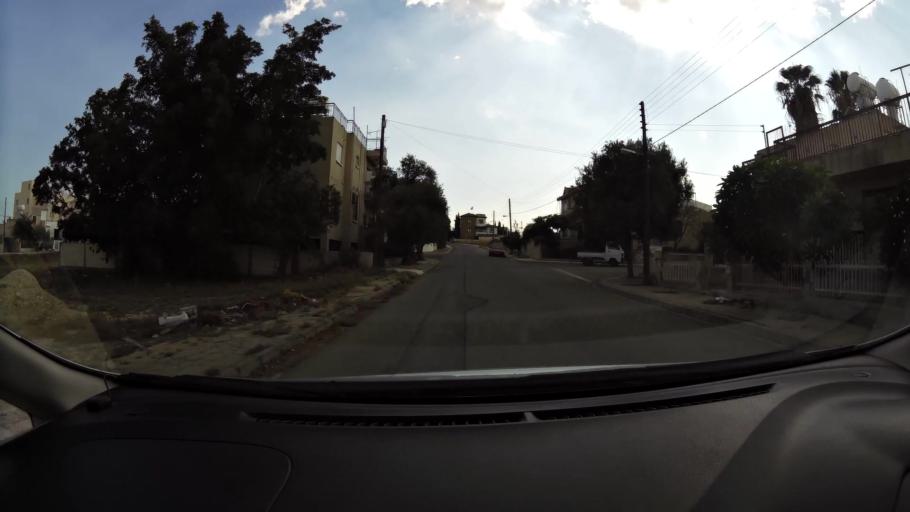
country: CY
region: Larnaka
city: Larnaca
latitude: 34.9102
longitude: 33.5918
